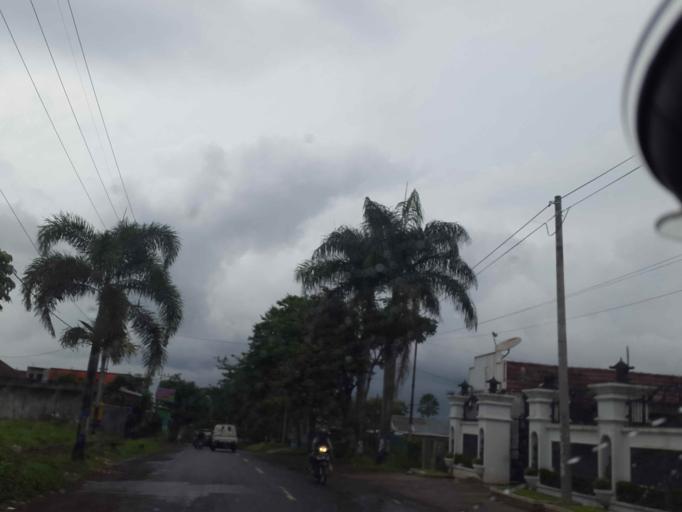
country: ID
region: East Java
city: Batu
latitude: -7.8647
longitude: 112.5406
